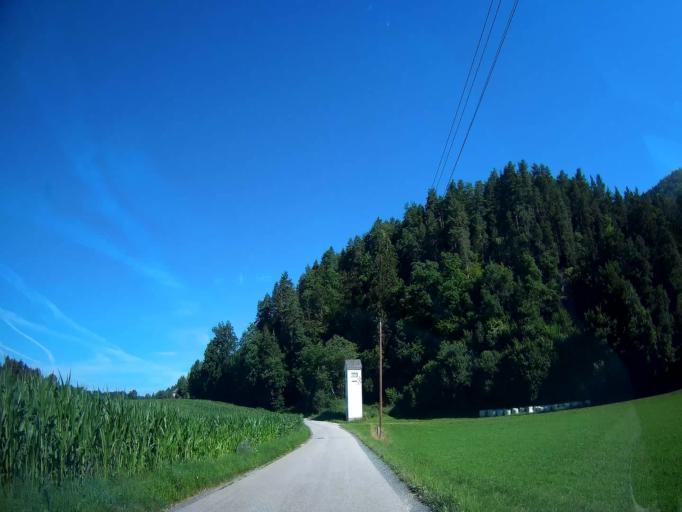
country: AT
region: Carinthia
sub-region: Politischer Bezirk Volkermarkt
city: Voelkermarkt
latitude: 46.6570
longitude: 14.5459
